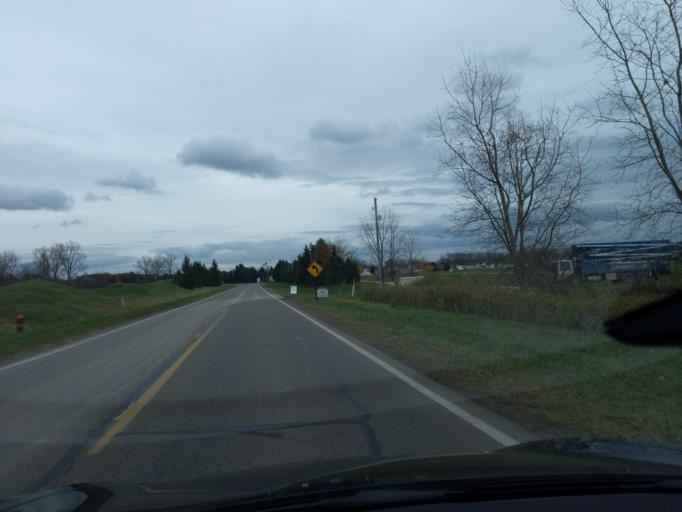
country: US
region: Michigan
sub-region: Ingham County
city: East Lansing
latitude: 42.7840
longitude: -84.4976
